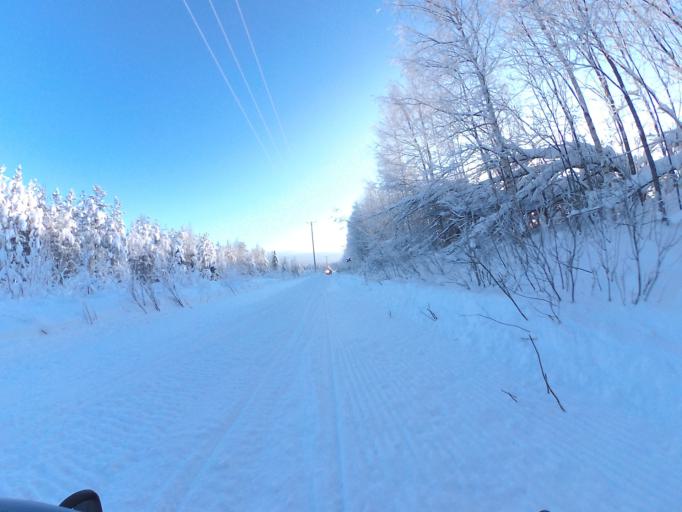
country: FI
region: Lapland
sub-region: Rovaniemi
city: Rovaniemi
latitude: 66.5463
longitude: 25.8626
